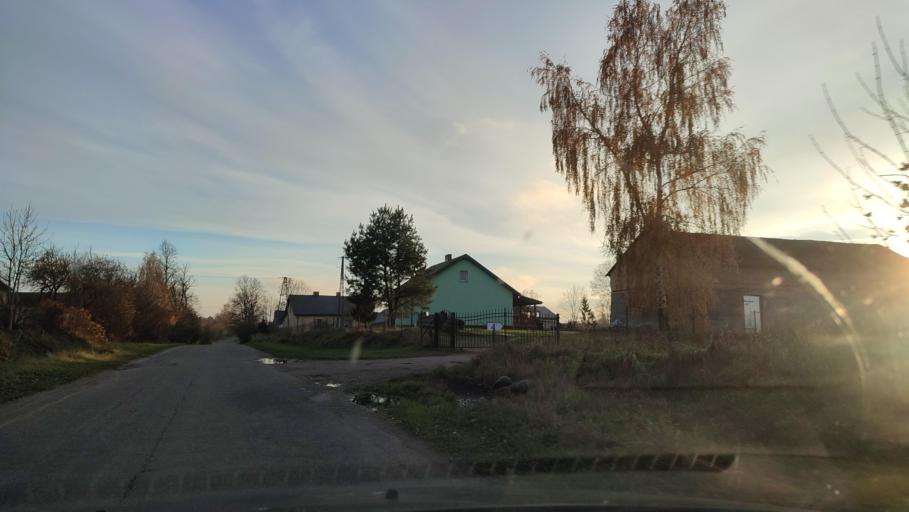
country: PL
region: Masovian Voivodeship
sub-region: Powiat mlawski
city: Wieczfnia Koscielna
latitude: 53.2462
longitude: 20.5814
